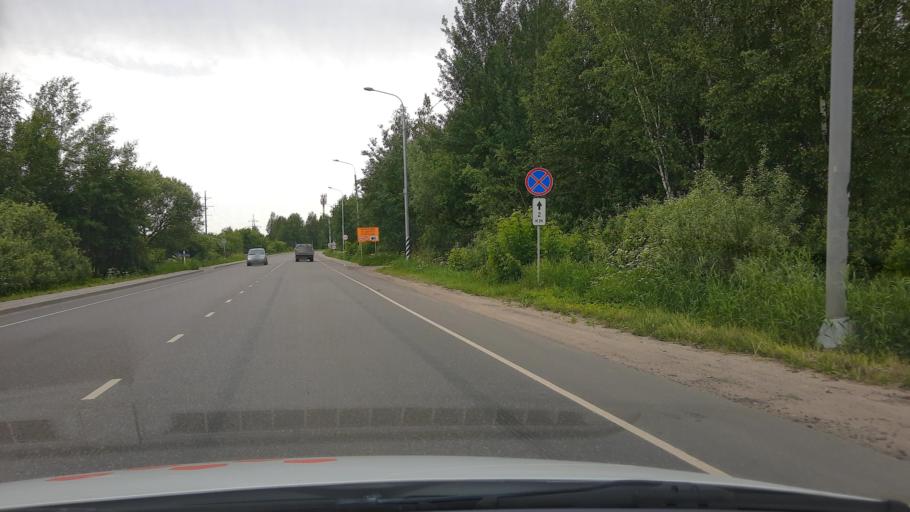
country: RU
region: Moskovskaya
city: Noginsk
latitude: 55.8578
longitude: 38.4071
